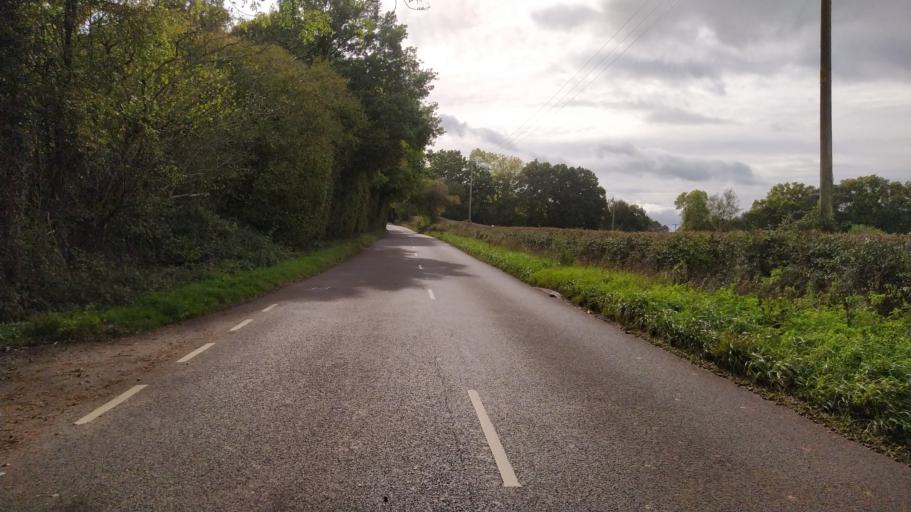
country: GB
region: England
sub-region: Hampshire
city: Romsey
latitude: 51.0237
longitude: -1.5399
